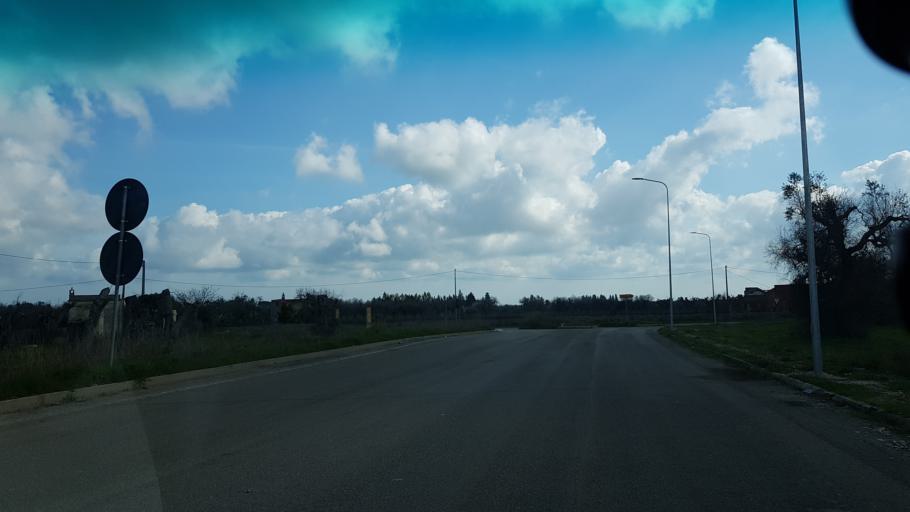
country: IT
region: Apulia
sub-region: Provincia di Lecce
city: Squinzano
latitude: 40.4487
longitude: 18.0401
